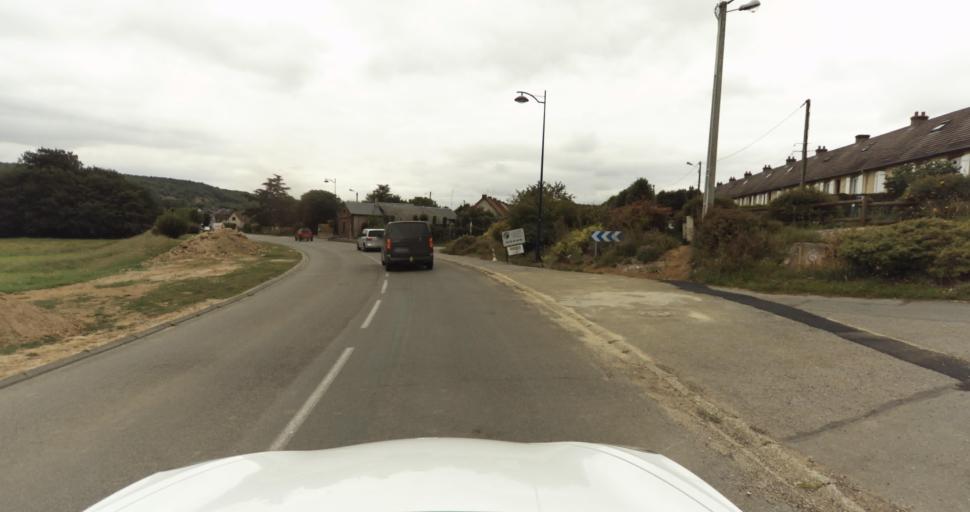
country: FR
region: Haute-Normandie
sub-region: Departement de l'Eure
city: Saint-Sebastien-de-Morsent
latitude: 48.9961
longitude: 1.0419
